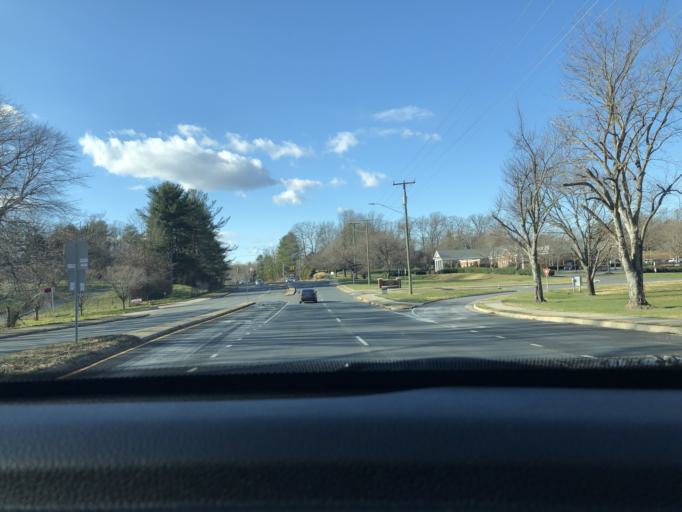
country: US
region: Virginia
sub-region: City of Fairfax
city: Fairfax
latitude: 38.8261
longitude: -77.2854
